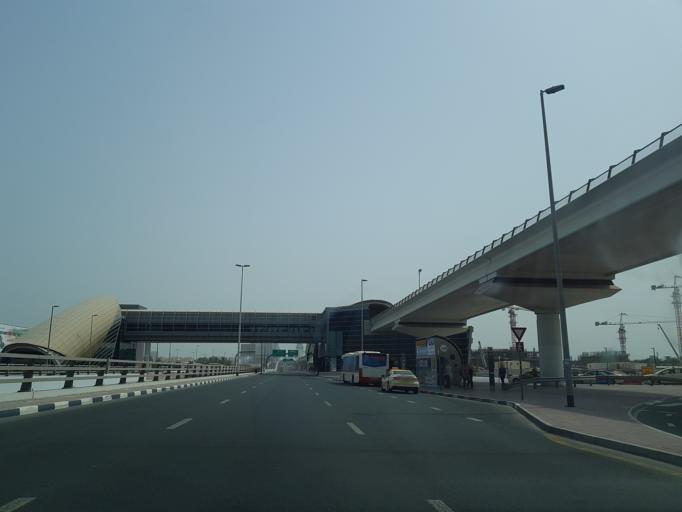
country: AE
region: Ash Shariqah
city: Sharjah
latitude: 25.2322
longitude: 55.2911
